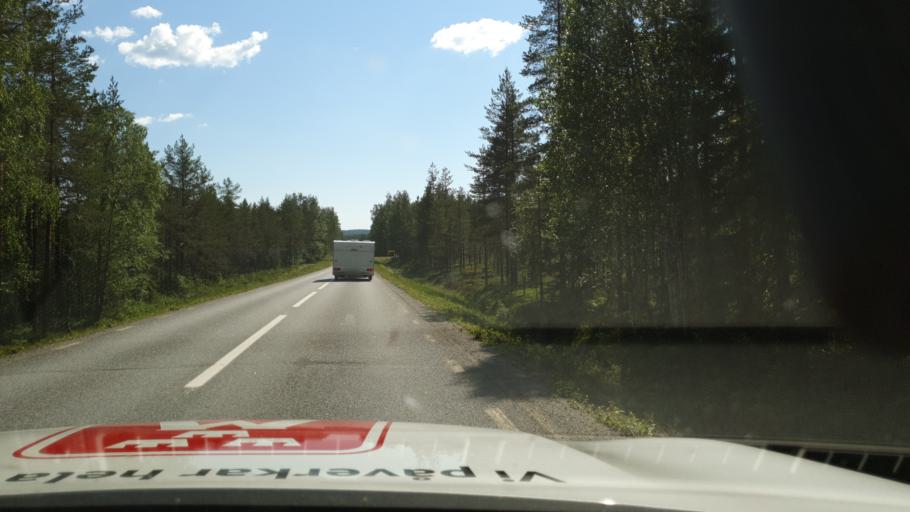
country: SE
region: Vaesterbotten
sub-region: Skelleftea Kommun
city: Burtraesk
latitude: 64.3510
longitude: 20.2388
